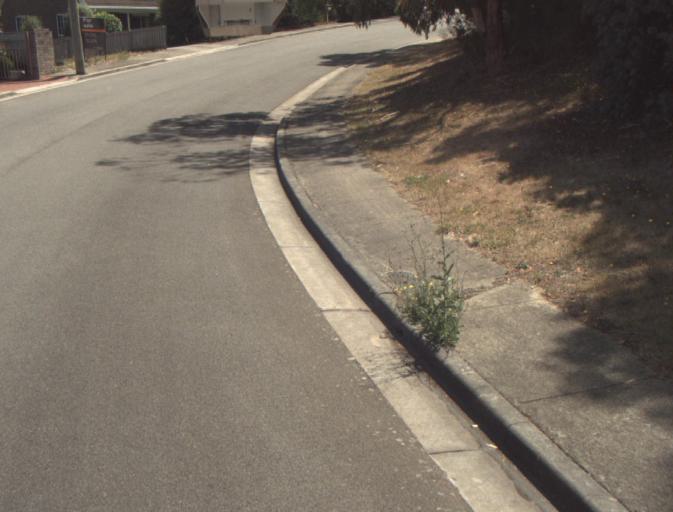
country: AU
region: Tasmania
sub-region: Launceston
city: Mayfield
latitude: -41.3802
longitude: 147.1149
